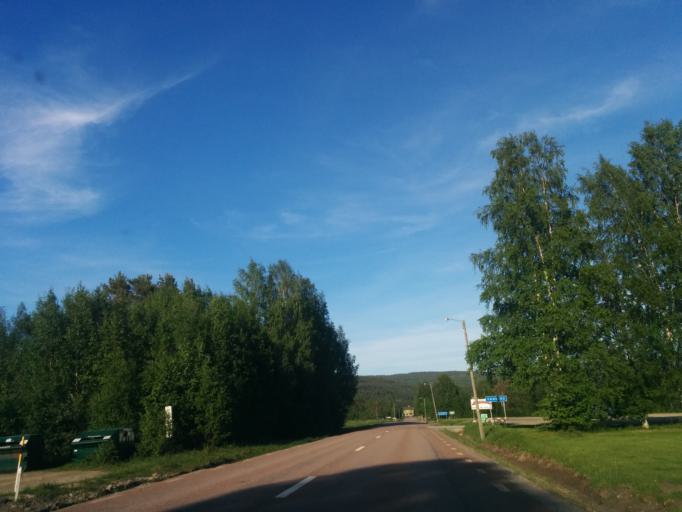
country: SE
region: Vaesternorrland
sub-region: Kramfors Kommun
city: Kramfors
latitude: 63.0227
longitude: 17.8062
